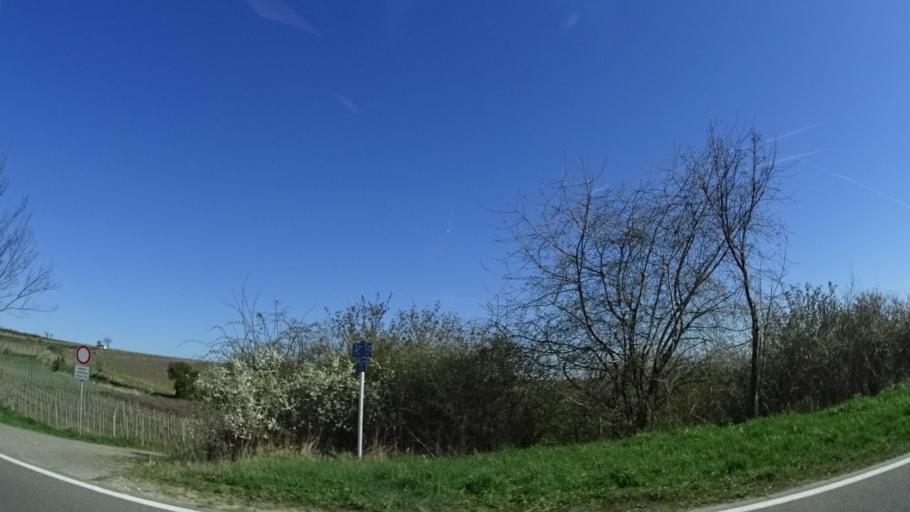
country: DE
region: Rheinland-Pfalz
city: Bechtheim
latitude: 49.7174
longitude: 8.3035
